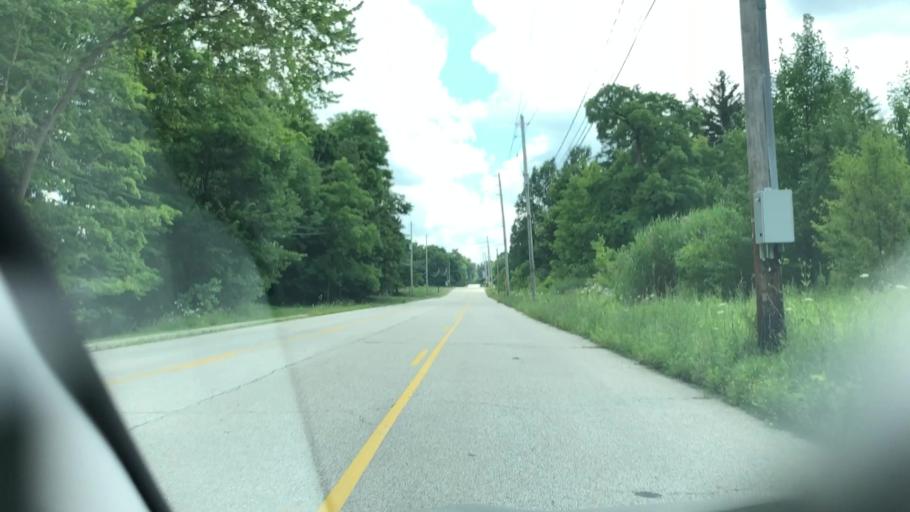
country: US
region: Ohio
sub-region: Summit County
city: Montrose-Ghent
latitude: 41.1286
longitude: -81.6485
